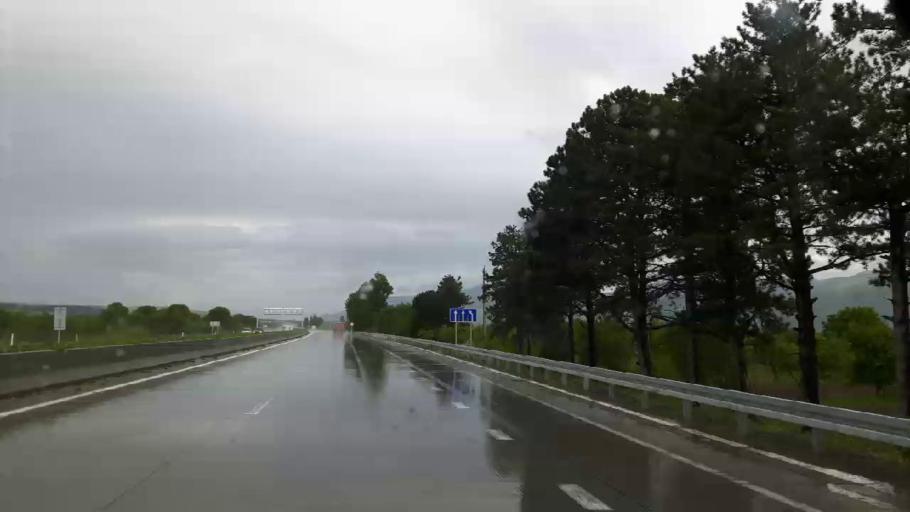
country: GE
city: Agara
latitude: 42.0308
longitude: 43.9519
